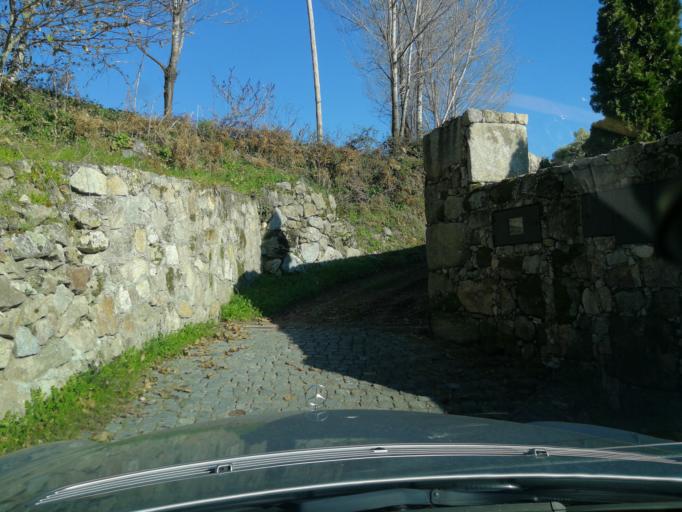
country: PT
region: Braga
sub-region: Braga
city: Adaufe
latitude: 41.6124
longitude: -8.3962
